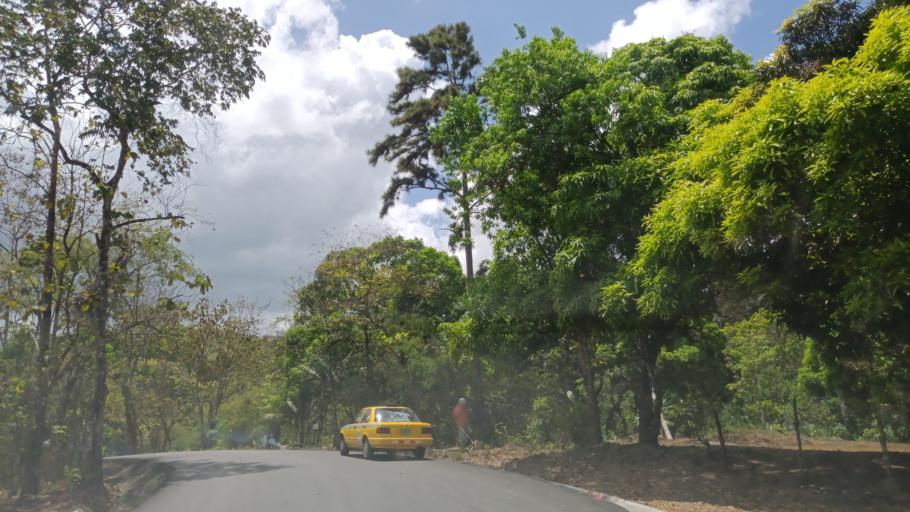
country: PA
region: Panama
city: Alcalde Diaz
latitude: 9.0862
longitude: -79.5786
